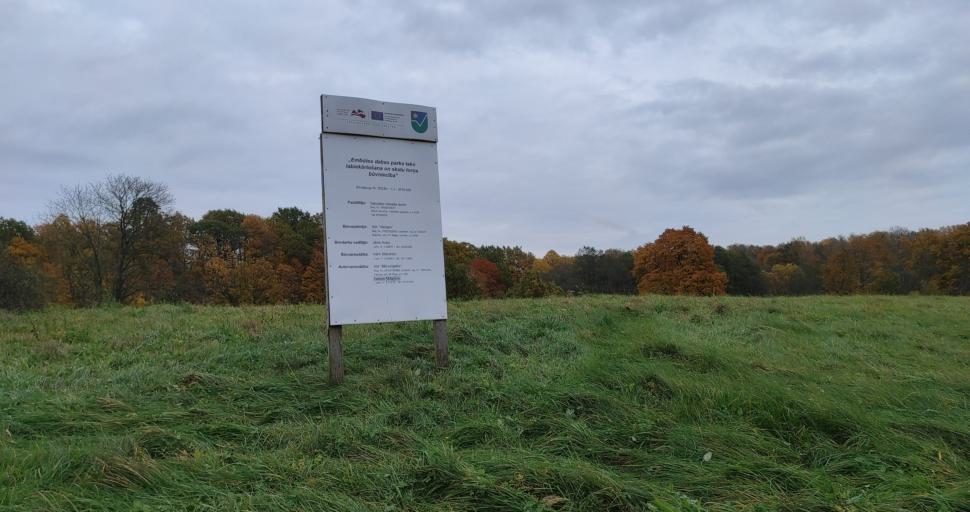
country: LV
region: Vainode
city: Vainode
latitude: 56.5098
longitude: 21.8170
